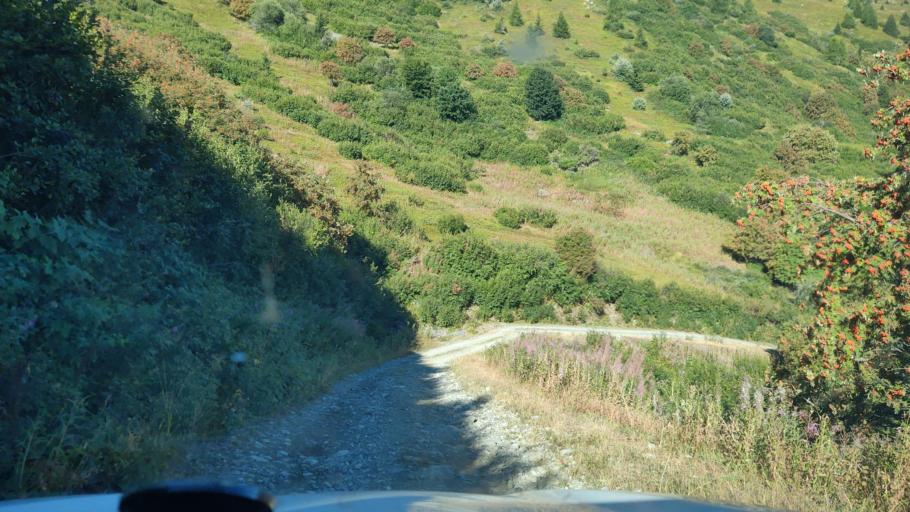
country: FR
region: Rhone-Alpes
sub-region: Departement de la Savoie
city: Valloire
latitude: 45.1739
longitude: 6.4676
